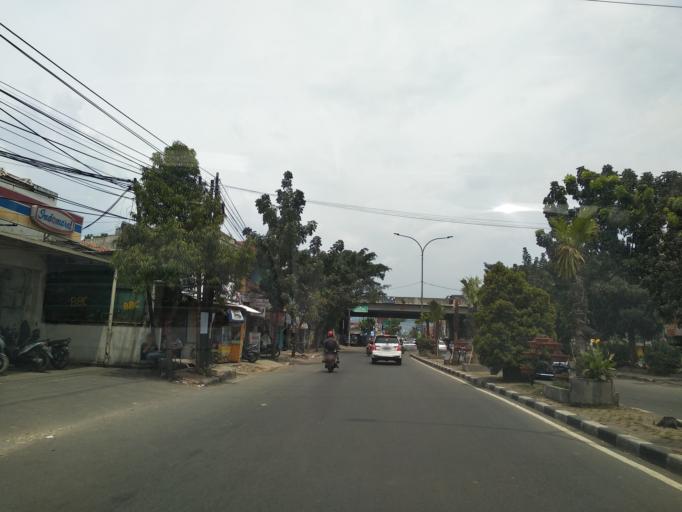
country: ID
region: West Java
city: Pameungpeuk
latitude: -6.9649
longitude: 107.6381
